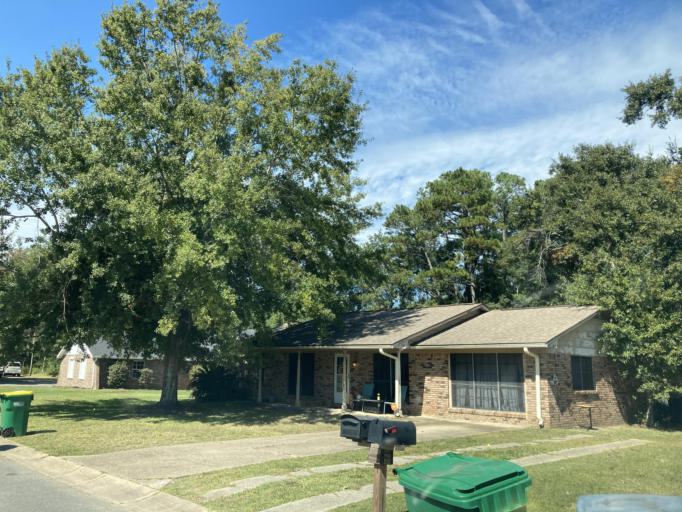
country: US
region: Mississippi
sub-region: Jackson County
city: Saint Martin
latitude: 30.4513
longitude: -88.8827
